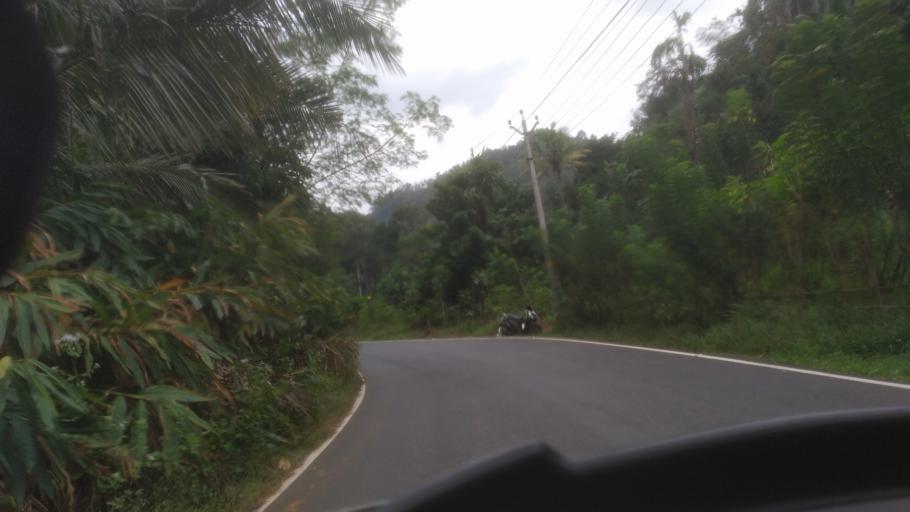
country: IN
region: Kerala
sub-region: Idukki
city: Idukki
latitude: 9.9681
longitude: 77.0013
